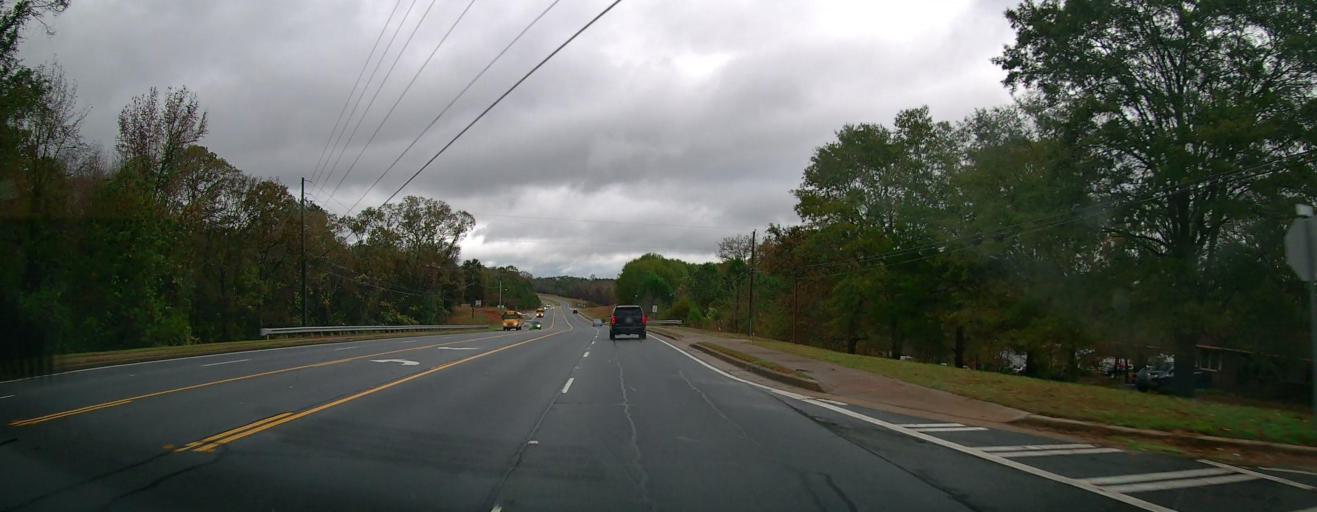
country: US
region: Georgia
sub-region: Jackson County
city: Nicholson
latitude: 34.1212
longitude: -83.4305
